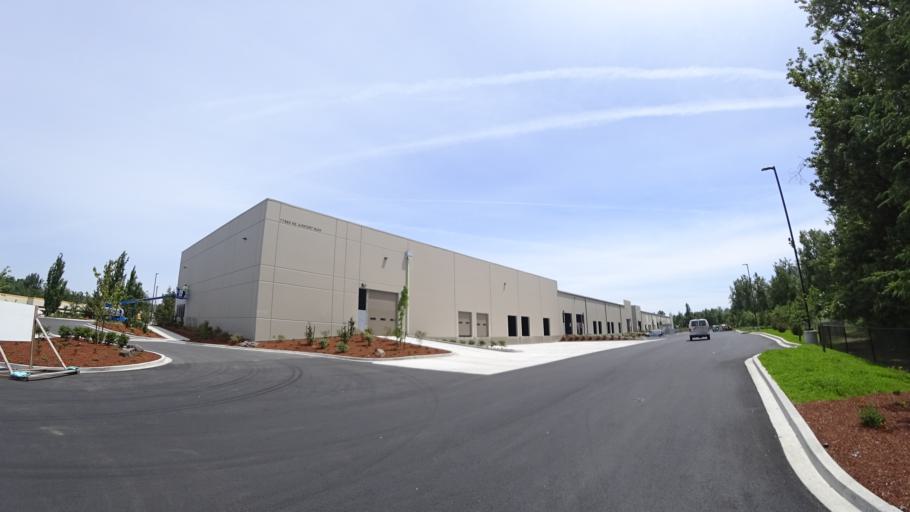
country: US
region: Oregon
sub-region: Multnomah County
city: Fairview
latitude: 45.5525
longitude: -122.4811
